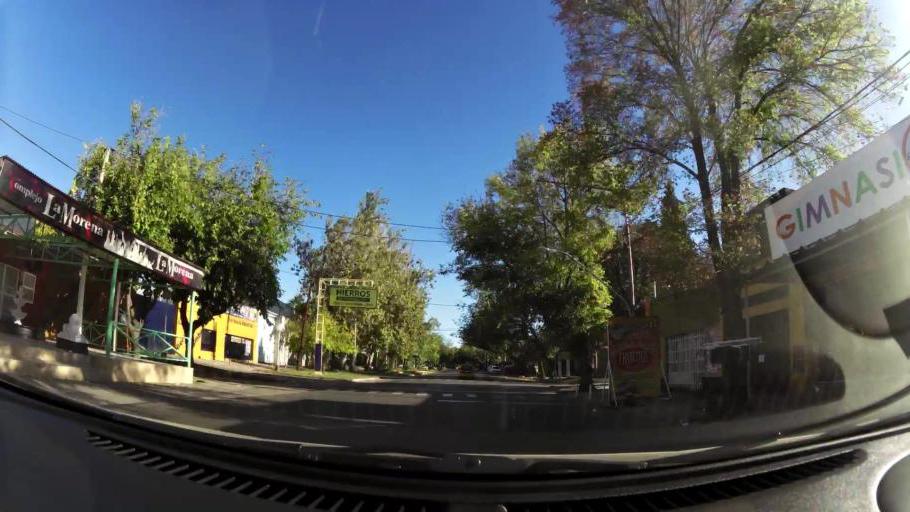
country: AR
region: Mendoza
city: Las Heras
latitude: -32.8634
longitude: -68.8283
